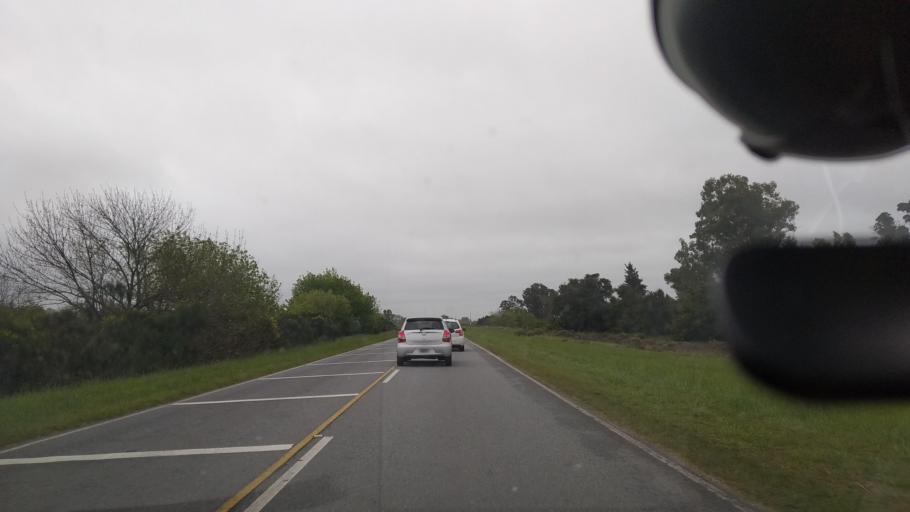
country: AR
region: Buenos Aires
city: Veronica
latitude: -35.3989
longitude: -57.3546
